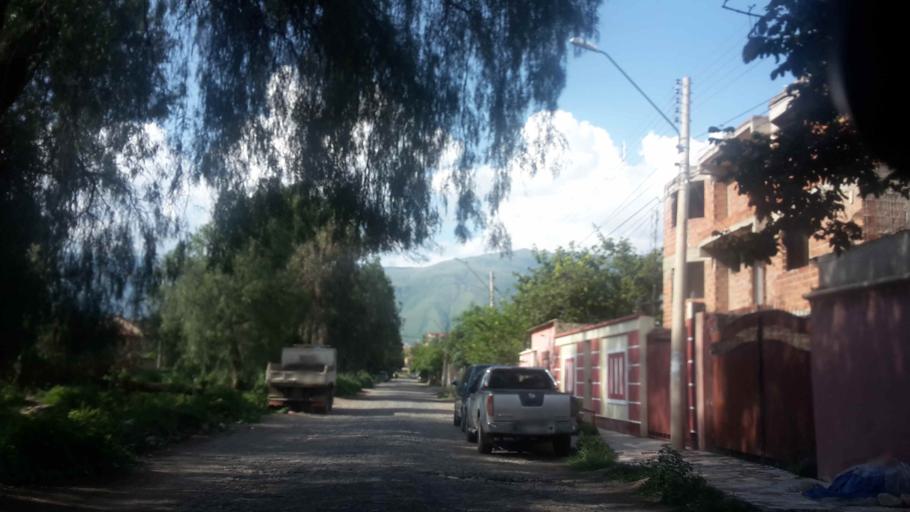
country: BO
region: Cochabamba
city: Cochabamba
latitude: -17.3797
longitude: -66.1960
